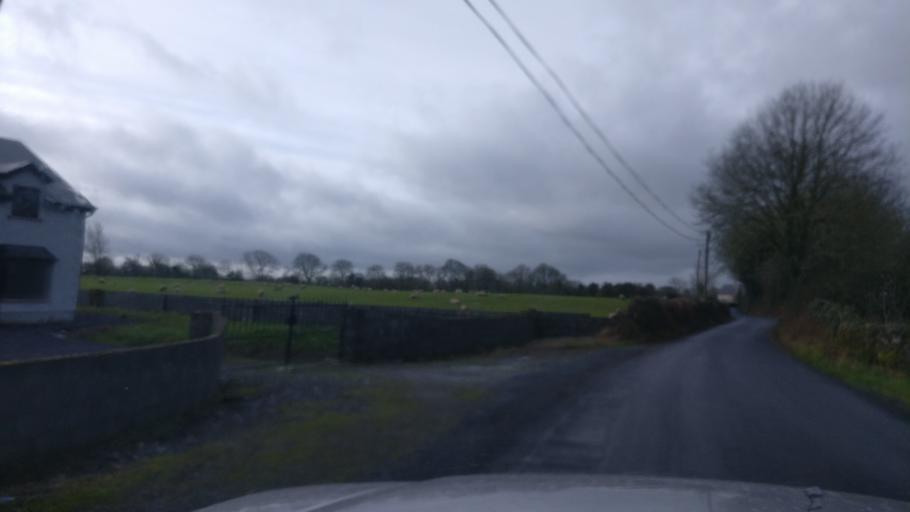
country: IE
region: Connaught
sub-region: County Galway
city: Athenry
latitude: 53.2679
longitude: -8.7767
